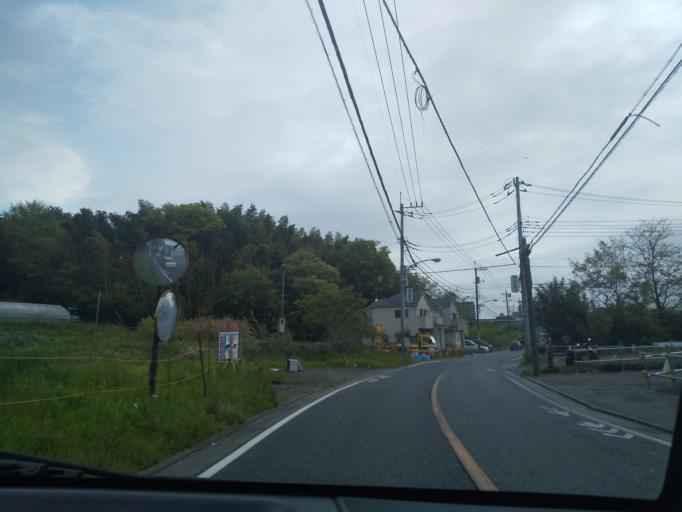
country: JP
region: Tokyo
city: Chofugaoka
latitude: 35.6345
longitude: 139.4940
